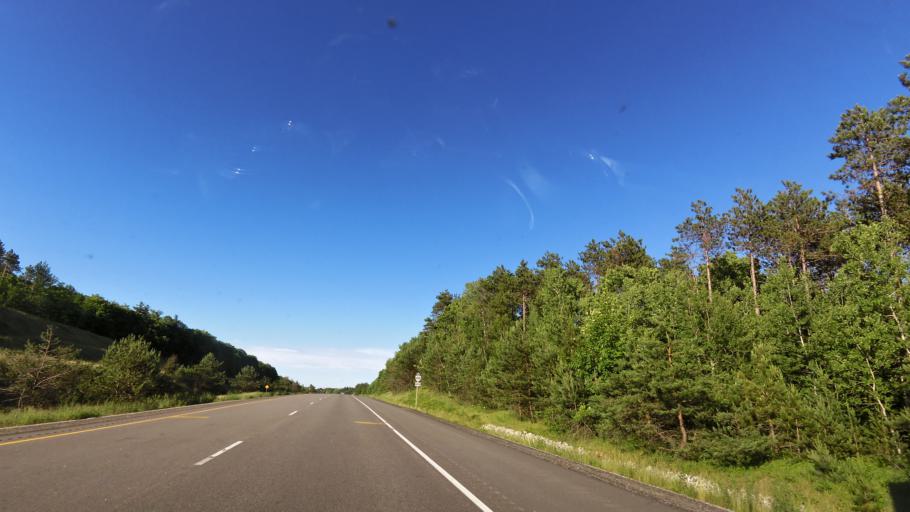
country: CA
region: Ontario
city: Barrie
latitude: 44.5830
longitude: -79.6968
